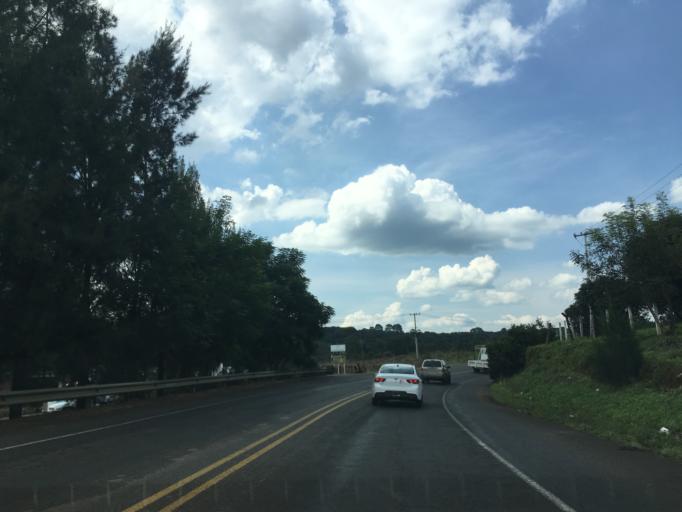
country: MX
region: Michoacan
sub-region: Tingueindin
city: Tingueindin
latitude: 19.7497
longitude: -102.4874
